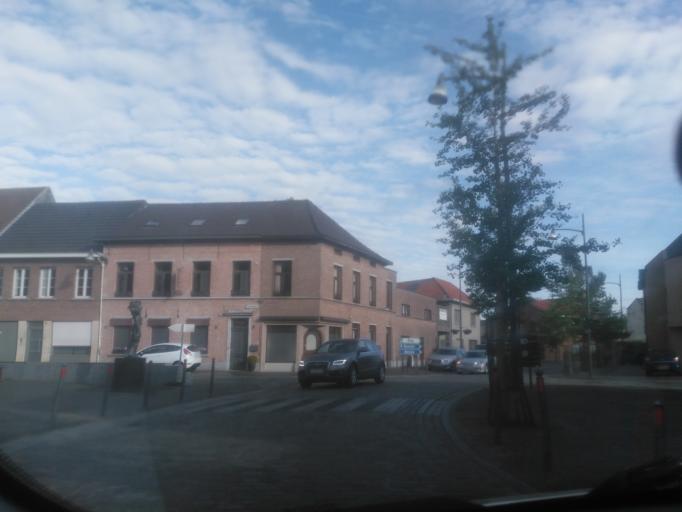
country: BE
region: Flanders
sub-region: Provincie Oost-Vlaanderen
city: Beveren
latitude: 51.2527
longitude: 4.2786
